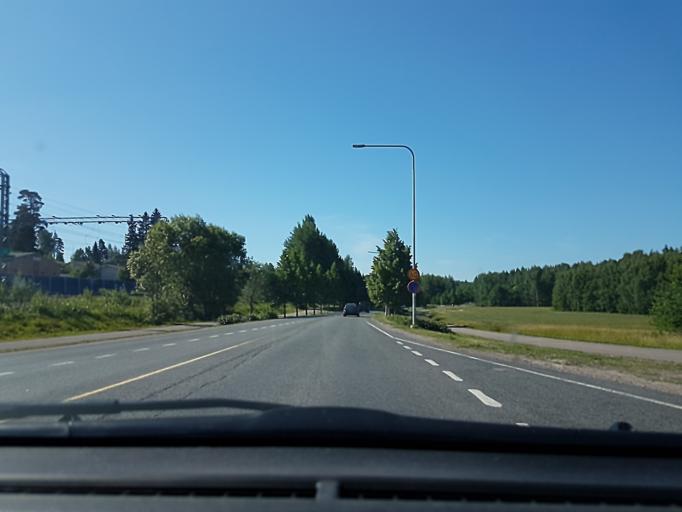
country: FI
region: Uusimaa
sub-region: Helsinki
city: Vantaa
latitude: 60.3450
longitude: 25.0742
